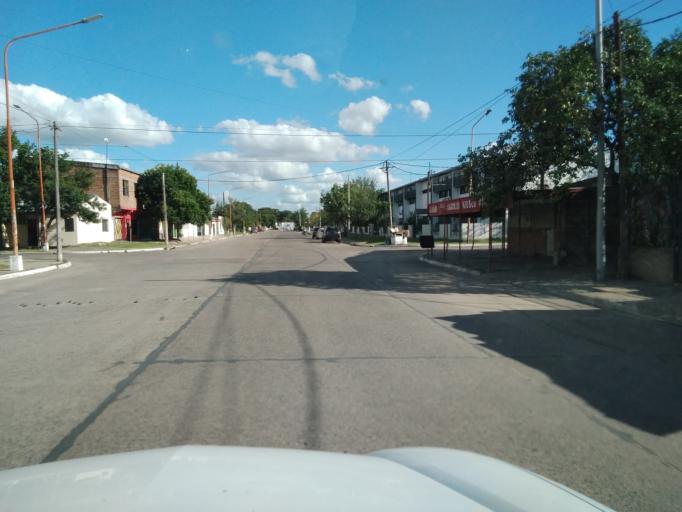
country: AR
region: Corrientes
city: Corrientes
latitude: -27.4957
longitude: -58.8340
